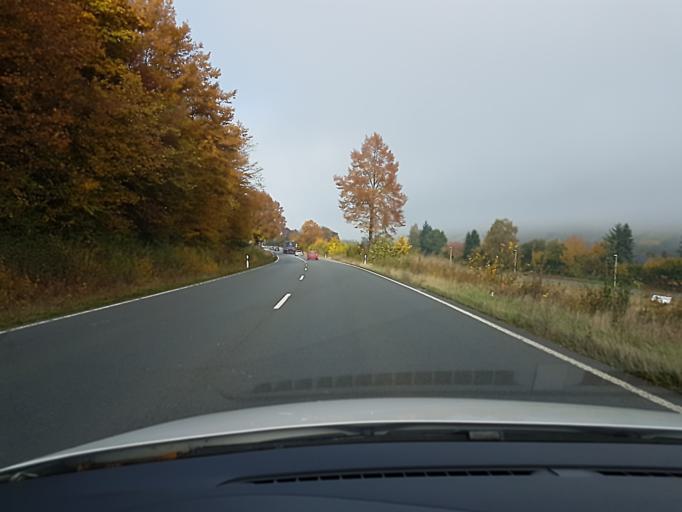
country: DE
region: Bavaria
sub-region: Regierungsbezirk Unterfranken
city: Kleinheubach
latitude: 49.7228
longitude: 9.2025
